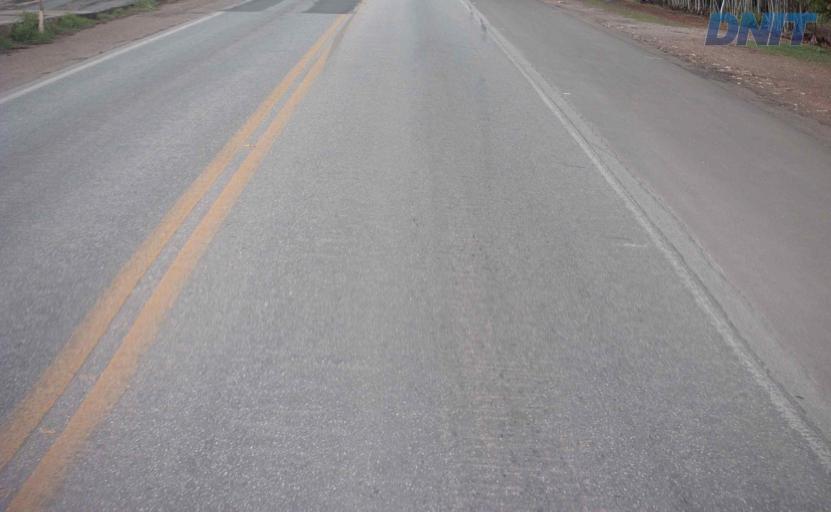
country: BR
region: Goias
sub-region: Uruacu
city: Uruacu
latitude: -14.6230
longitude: -49.1720
